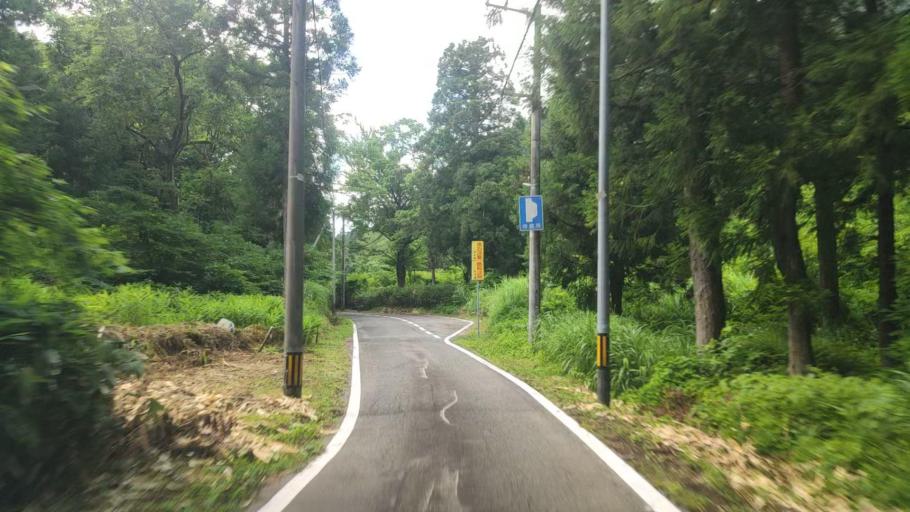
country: JP
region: Fukui
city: Katsuyama
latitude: 36.2036
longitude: 136.5252
